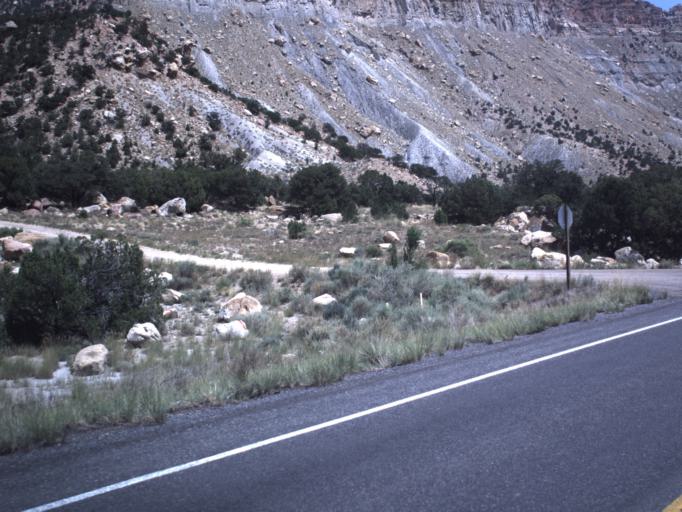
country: US
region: Utah
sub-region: Emery County
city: Huntington
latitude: 39.3884
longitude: -111.0862
